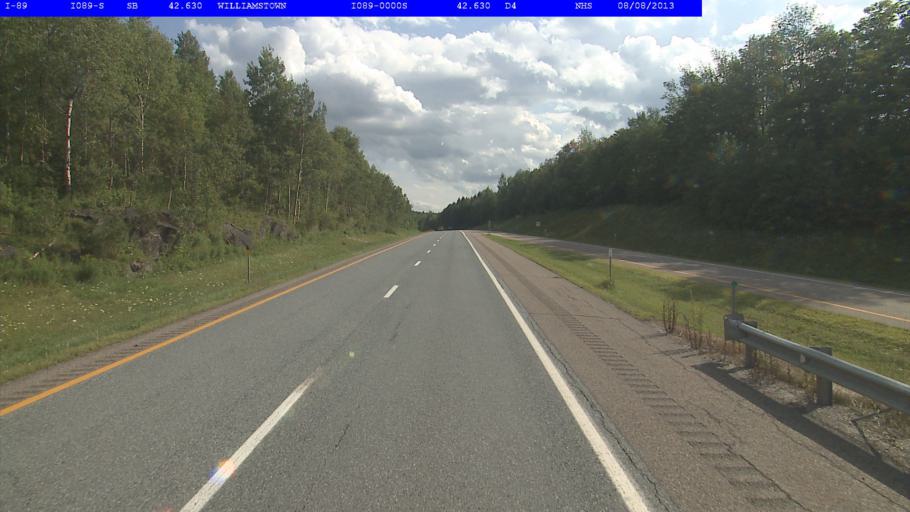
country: US
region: Vermont
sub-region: Washington County
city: Northfield
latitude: 44.1110
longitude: -72.6108
